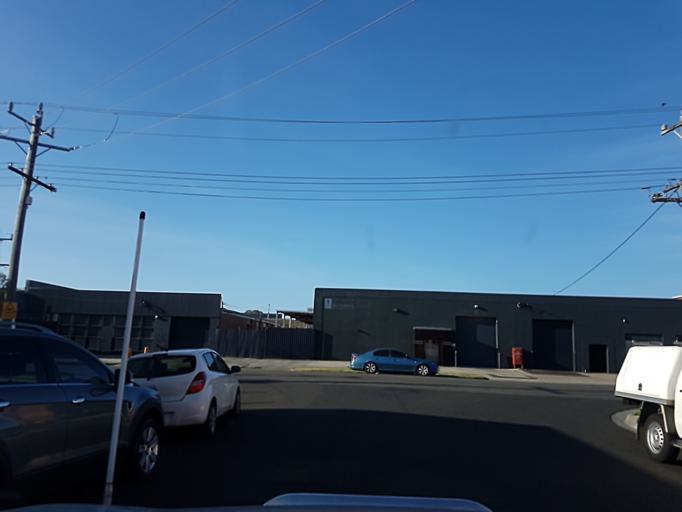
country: AU
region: Victoria
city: Highett
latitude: -37.9419
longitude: 145.0687
